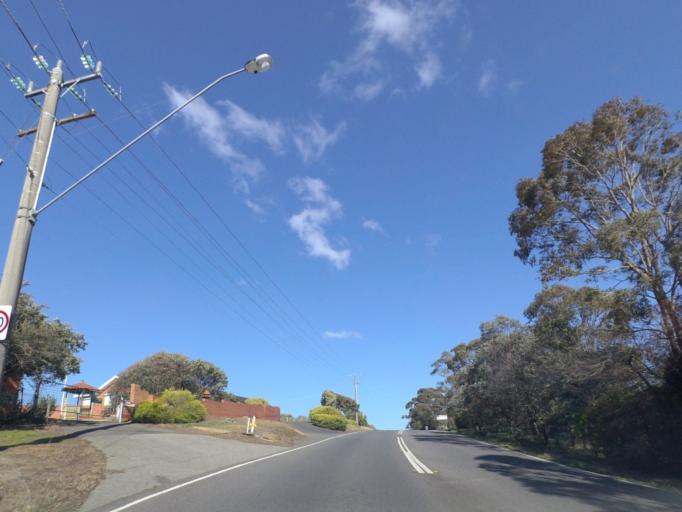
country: AU
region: Victoria
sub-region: Manningham
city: Park Orchards
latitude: -37.7676
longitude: 145.1999
